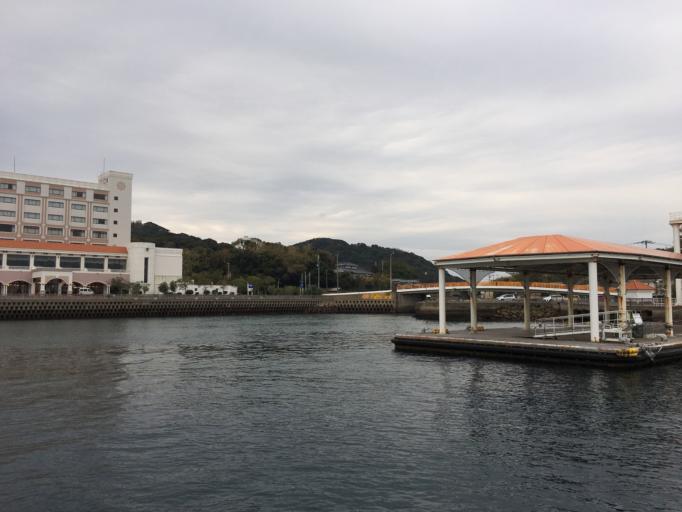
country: JP
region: Nagasaki
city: Nagasaki-shi
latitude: 32.7033
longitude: 129.7805
